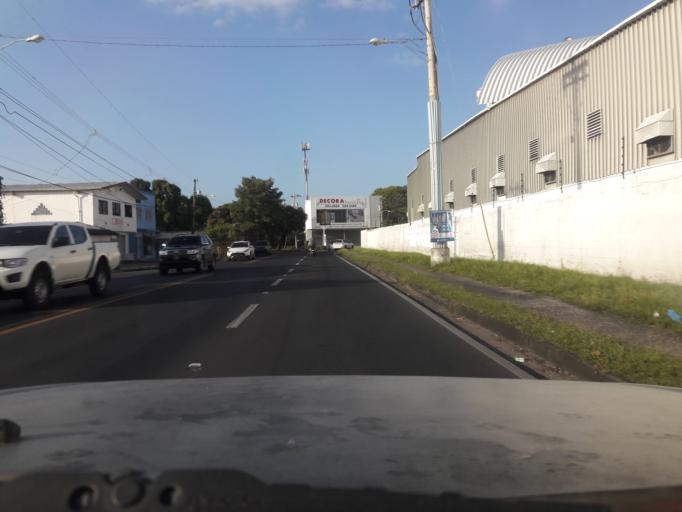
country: PA
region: Panama
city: San Miguelito
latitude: 9.0238
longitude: -79.4971
